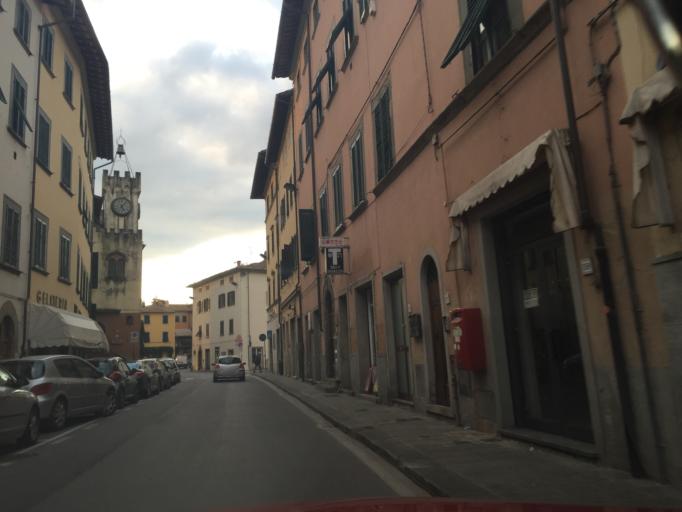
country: IT
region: Tuscany
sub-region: Provincia di Pistoia
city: Borgo a Buggiano
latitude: 43.8797
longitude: 10.7287
